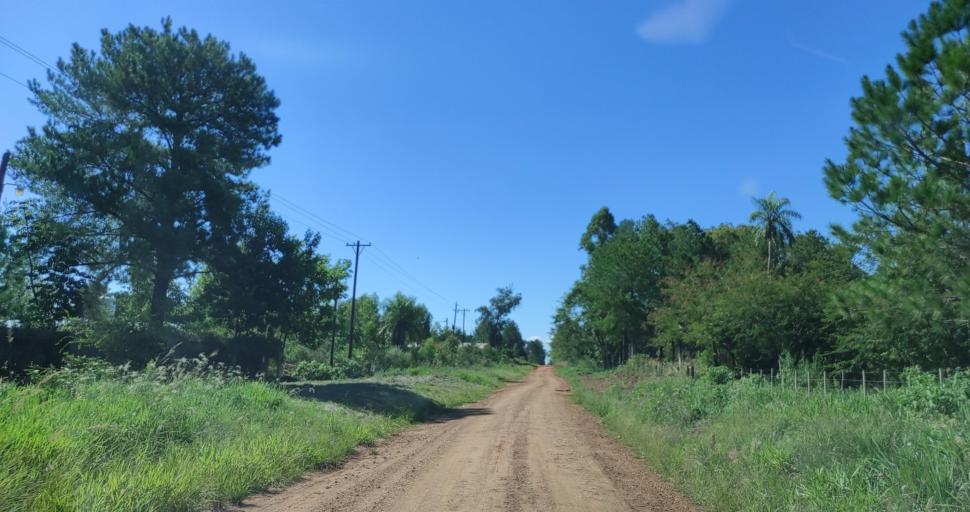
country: AR
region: Misiones
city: Garupa
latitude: -27.4713
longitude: -55.7982
